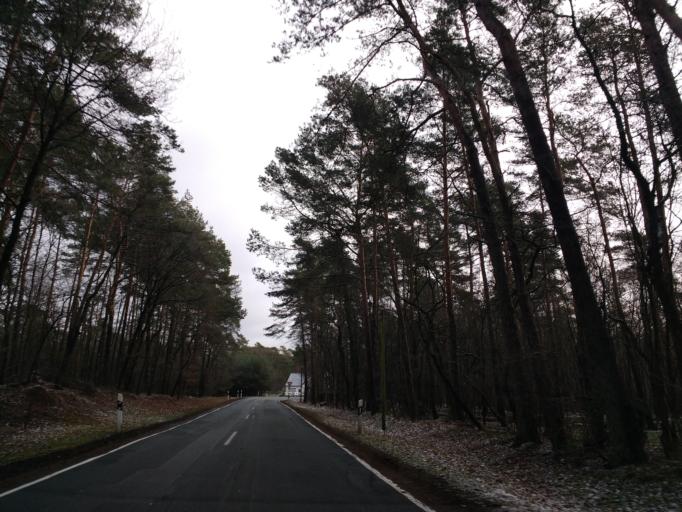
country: DE
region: North Rhine-Westphalia
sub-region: Regierungsbezirk Detmold
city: Augustdorf
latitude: 51.8707
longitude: 8.6953
